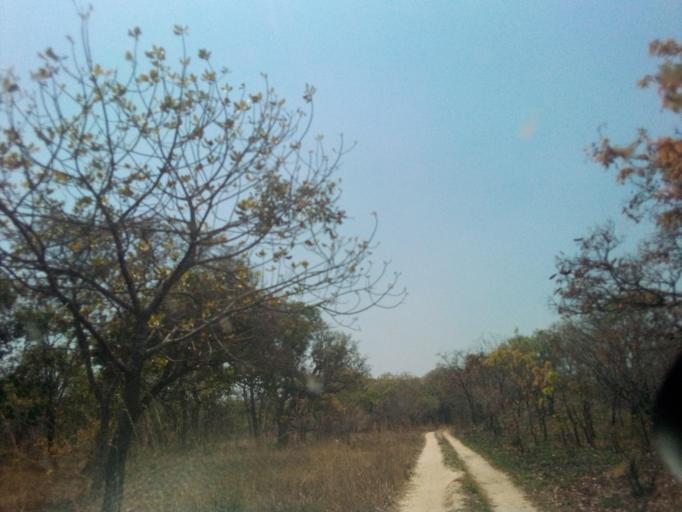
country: ZM
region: Copperbelt
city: Kataba
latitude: -12.2379
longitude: 30.4050
